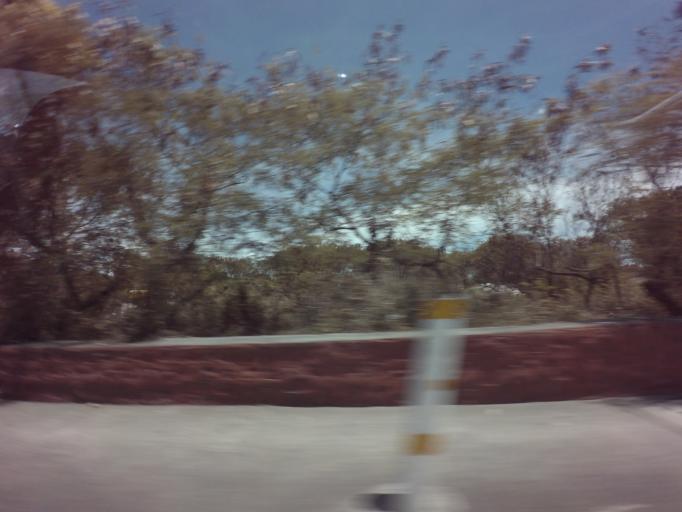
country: PH
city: Sambayanihan People's Village
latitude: 14.4908
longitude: 120.9981
